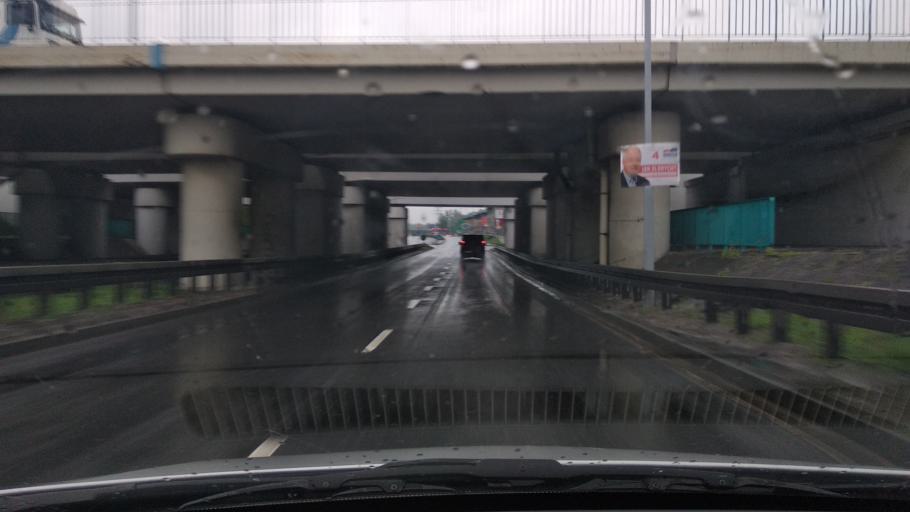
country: PL
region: Silesian Voivodeship
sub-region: Katowice
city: Katowice
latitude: 50.2641
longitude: 18.9877
